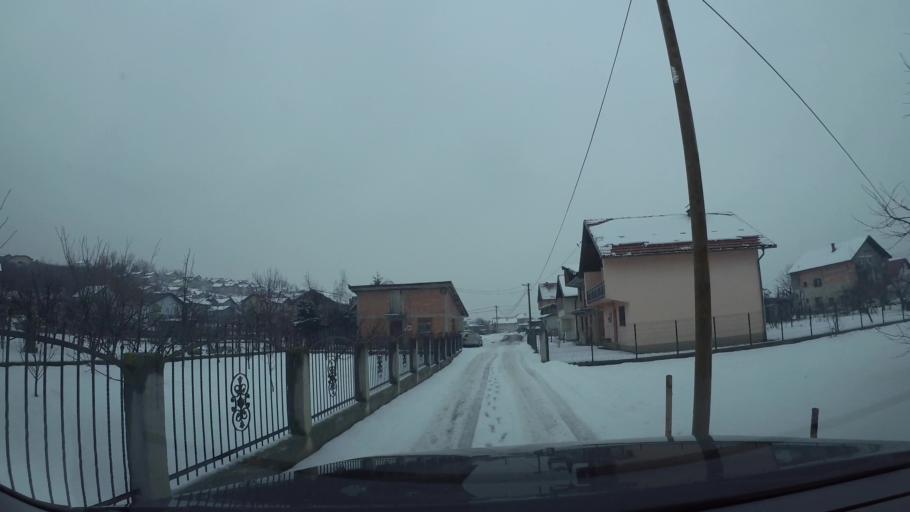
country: BA
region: Federation of Bosnia and Herzegovina
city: Hadzici
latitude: 43.8416
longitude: 18.2707
